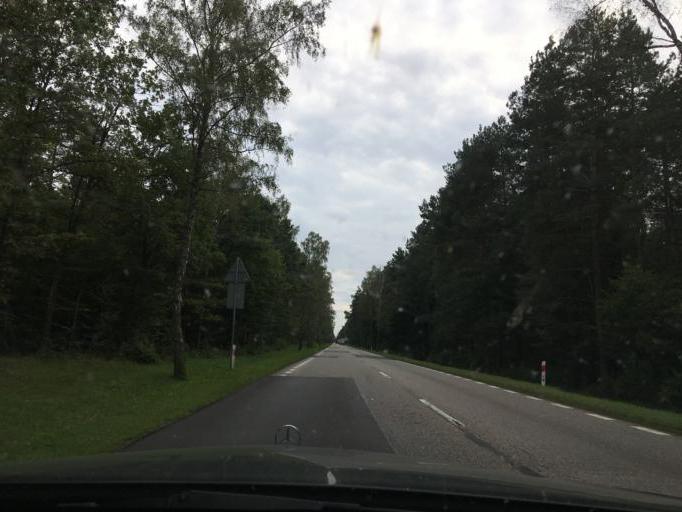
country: PL
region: Podlasie
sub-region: Powiat kolnenski
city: Stawiski
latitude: 53.3480
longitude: 22.1592
